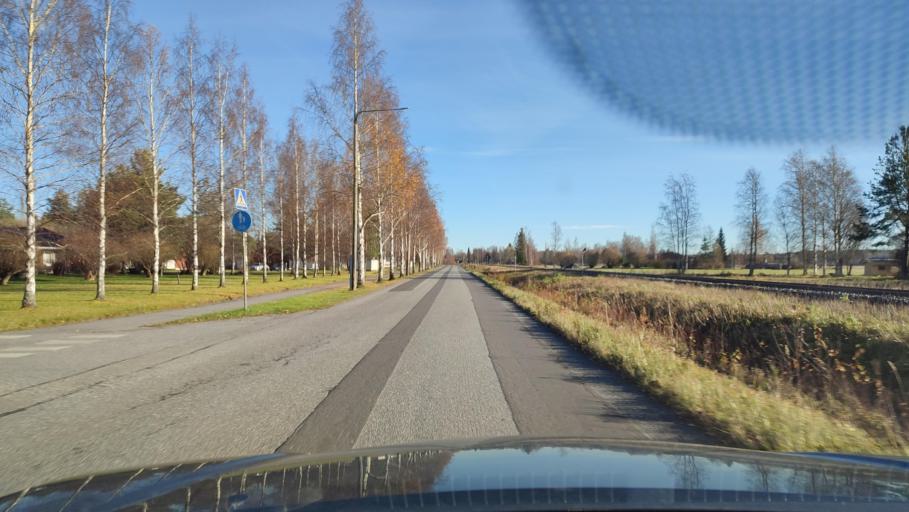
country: FI
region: Southern Ostrobothnia
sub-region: Suupohja
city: Teuva
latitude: 62.4715
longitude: 21.7245
